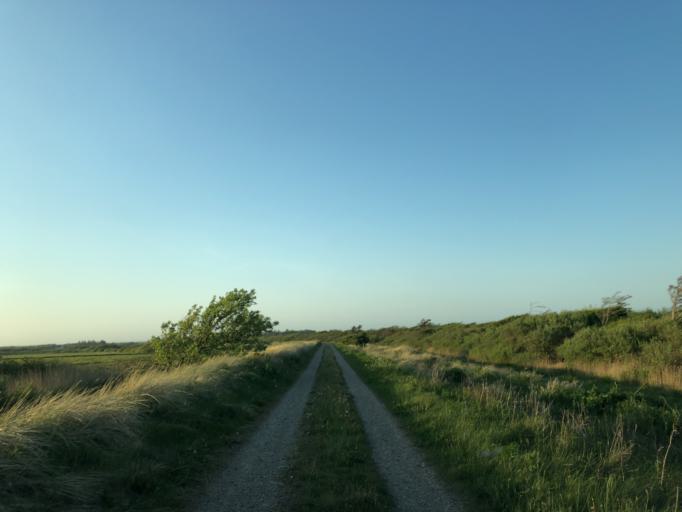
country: DK
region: Central Jutland
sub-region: Holstebro Kommune
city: Ulfborg
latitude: 56.2431
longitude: 8.1628
